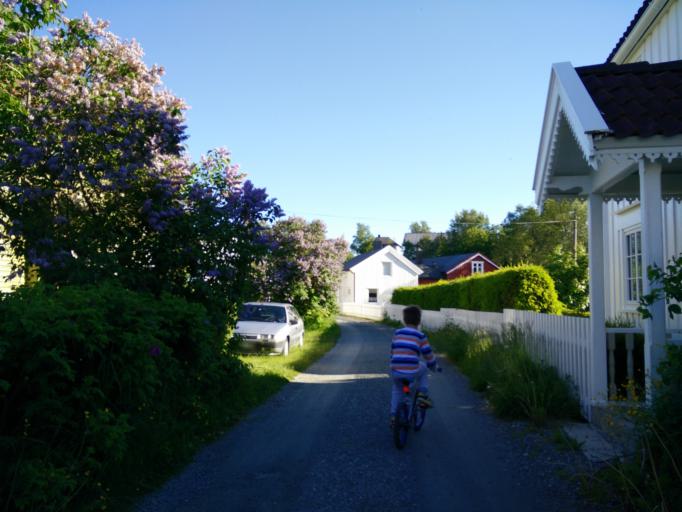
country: NO
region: Sor-Trondelag
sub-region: Skaun
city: Borsa
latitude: 63.3261
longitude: 10.0753
